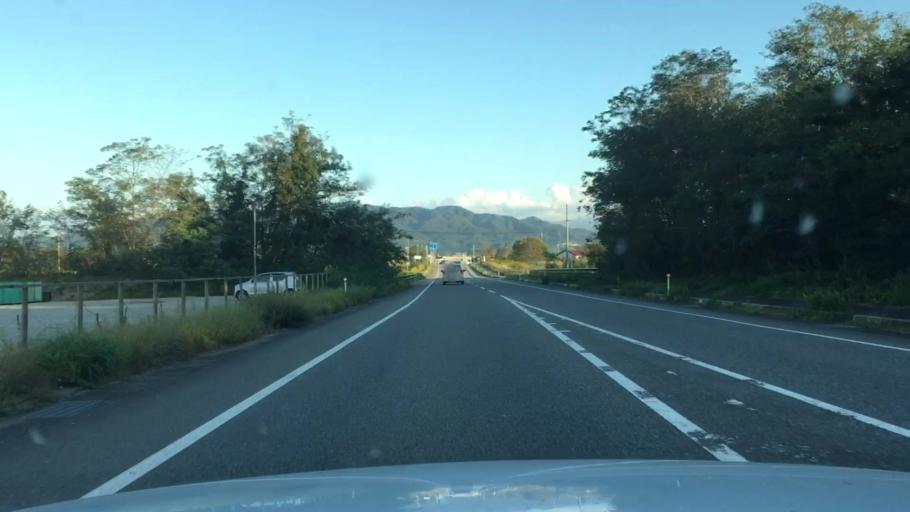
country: JP
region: Niigata
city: Murakami
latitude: 38.1233
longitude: 139.4051
